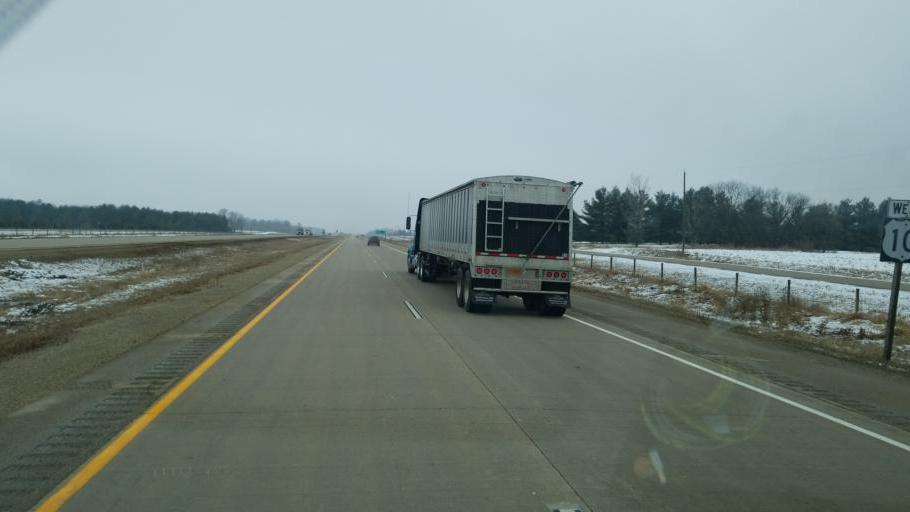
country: US
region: Wisconsin
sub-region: Winnebago County
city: Winneconne
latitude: 44.2343
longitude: -88.7491
